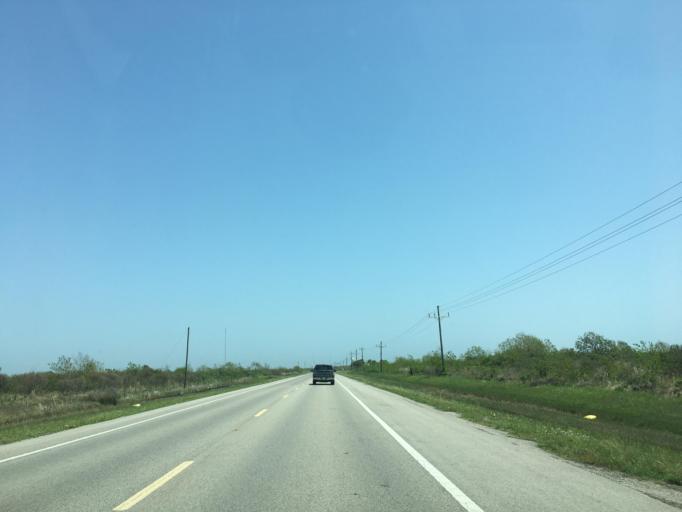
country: US
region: Texas
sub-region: Galveston County
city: Galveston
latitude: 29.4051
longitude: -94.7207
